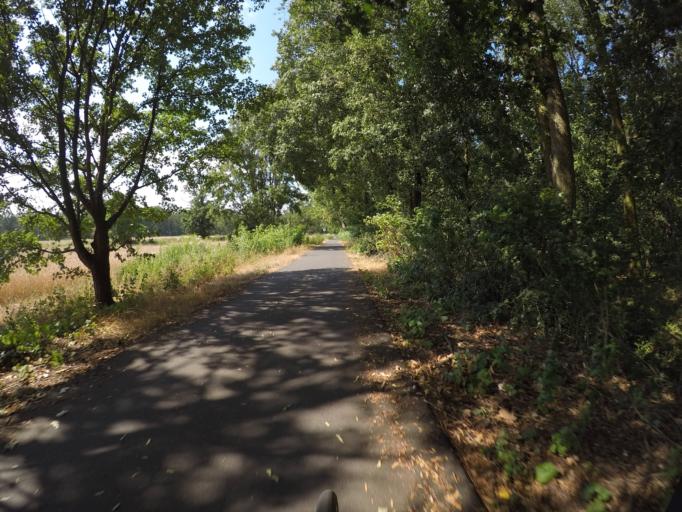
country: DE
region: Berlin
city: Kladow
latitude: 52.4919
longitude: 13.1457
